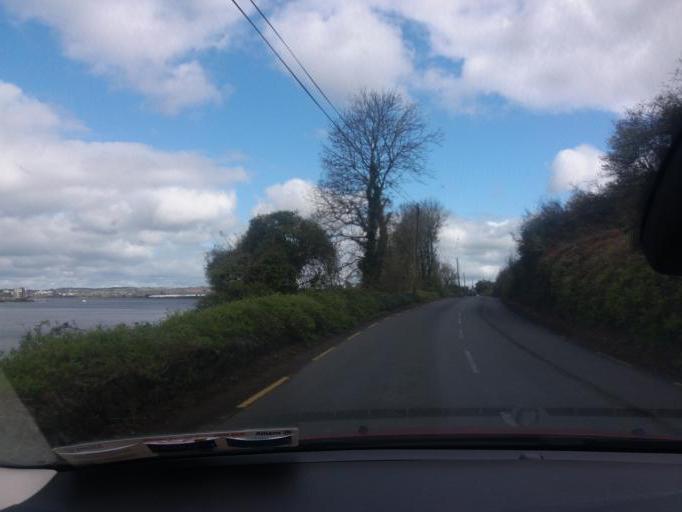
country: IE
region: Munster
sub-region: County Cork
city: Passage West
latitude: 51.8638
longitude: -8.3258
